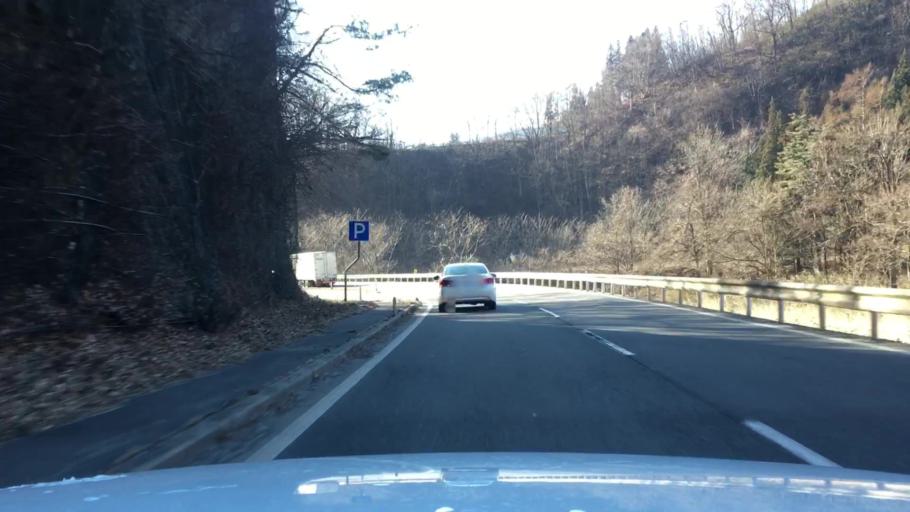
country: JP
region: Iwate
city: Miyako
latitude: 39.6101
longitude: 141.6495
